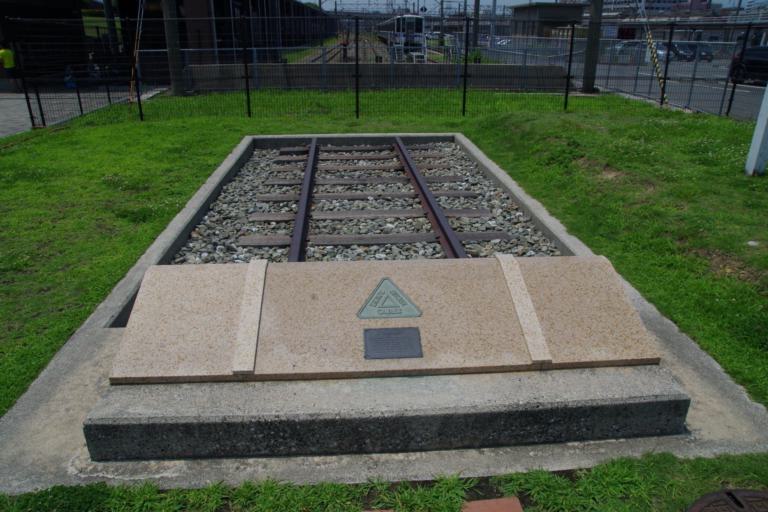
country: JP
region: Yamaguchi
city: Shimonoseki
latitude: 33.9440
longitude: 130.9631
